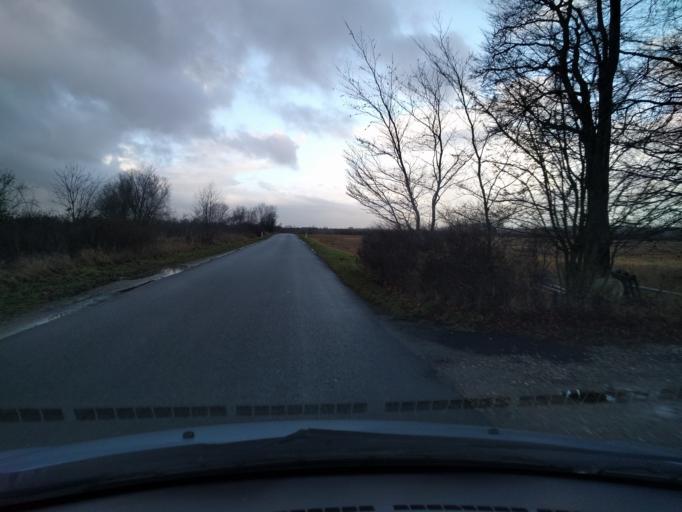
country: DK
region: South Denmark
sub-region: Kerteminde Kommune
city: Langeskov
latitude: 55.3773
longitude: 10.5810
